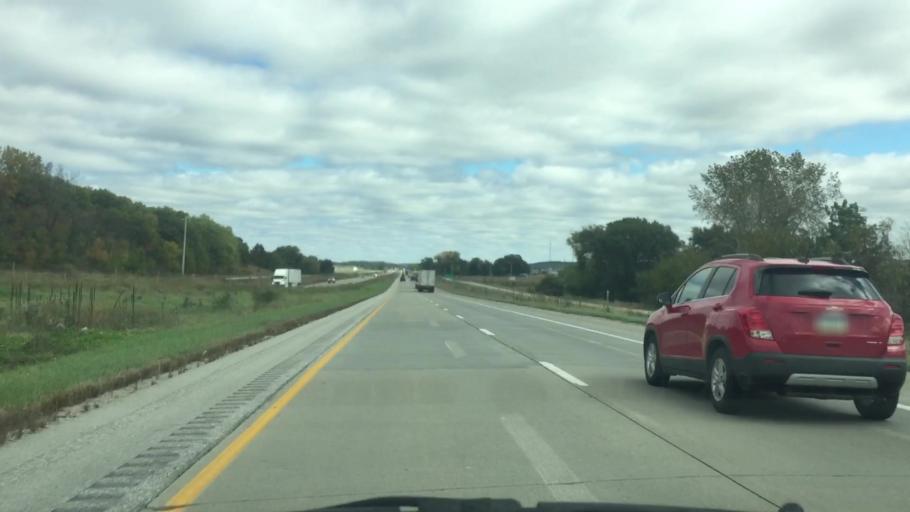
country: US
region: Iowa
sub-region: Jasper County
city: Colfax
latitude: 41.6881
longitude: -93.2734
